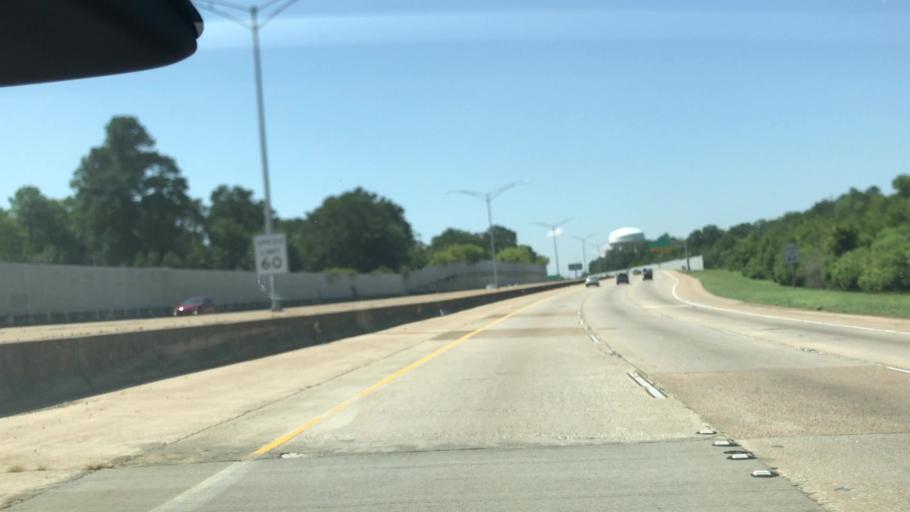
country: US
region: Louisiana
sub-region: Bossier Parish
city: Bossier City
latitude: 32.4665
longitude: -93.7555
